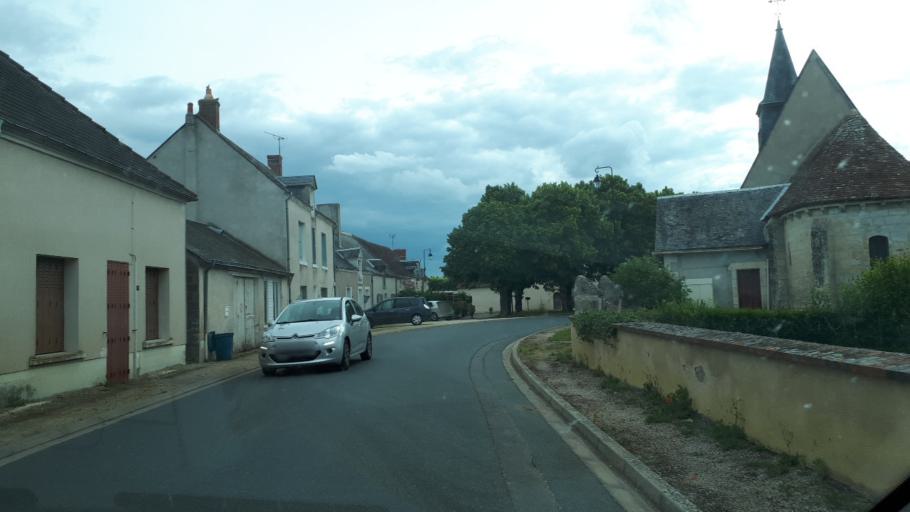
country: FR
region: Centre
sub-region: Departement du Cher
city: Massay
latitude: 47.0980
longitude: 1.9674
